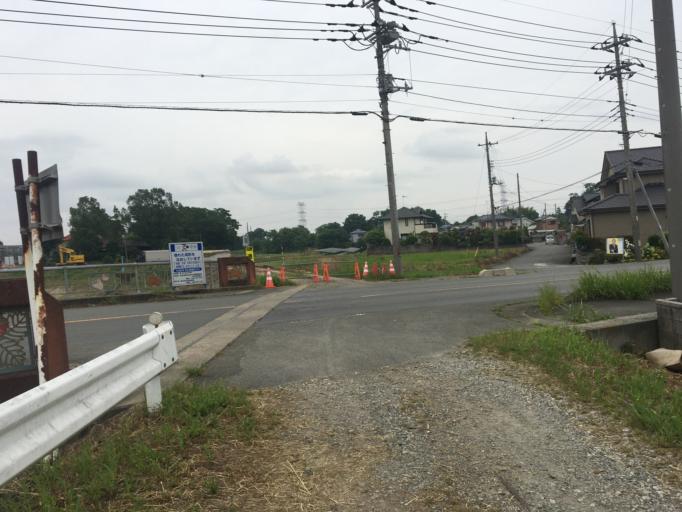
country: JP
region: Saitama
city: Sakado
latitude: 36.0035
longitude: 139.4380
